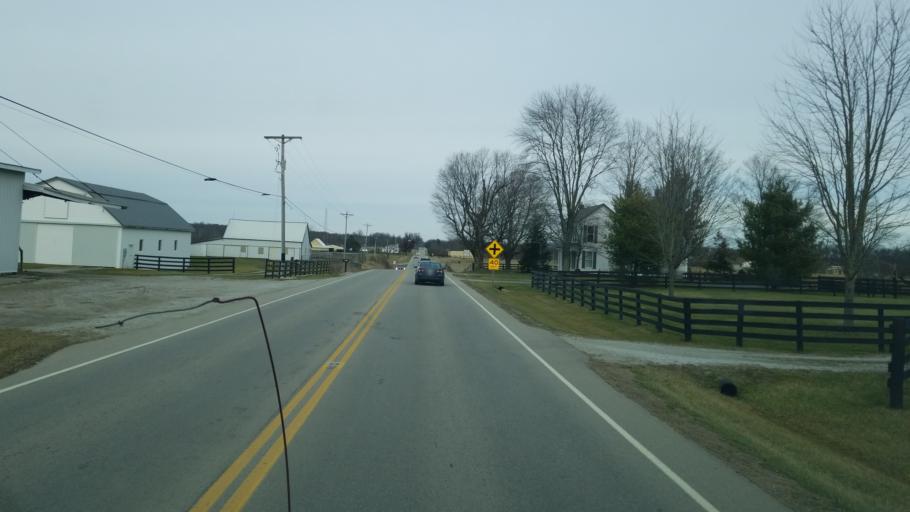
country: US
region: Ohio
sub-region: Adams County
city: Winchester
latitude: 39.0690
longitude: -83.6887
